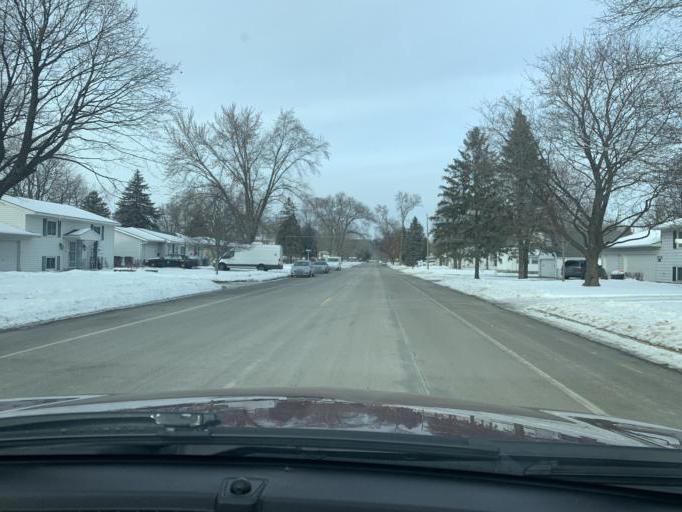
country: US
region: Minnesota
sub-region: Washington County
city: Saint Paul Park
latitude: 44.8376
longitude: -92.9841
